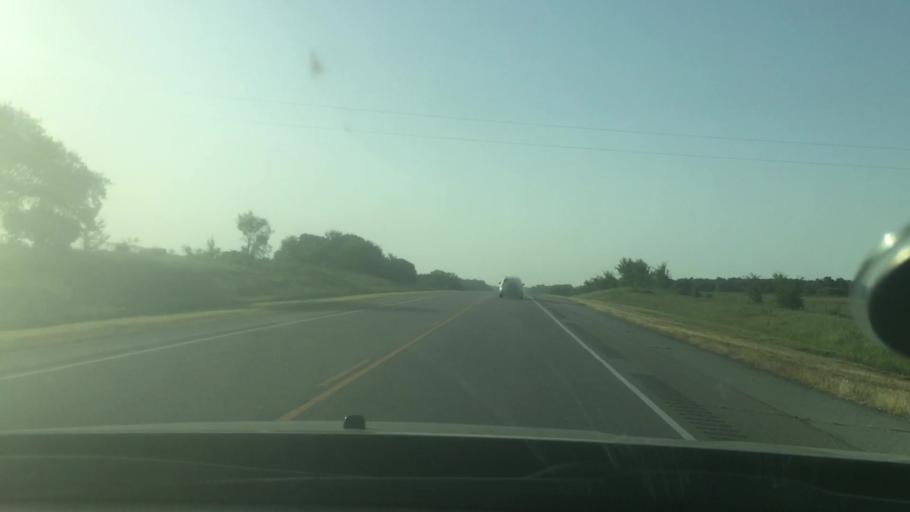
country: US
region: Oklahoma
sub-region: Pontotoc County
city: Ada
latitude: 34.6346
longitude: -96.4760
